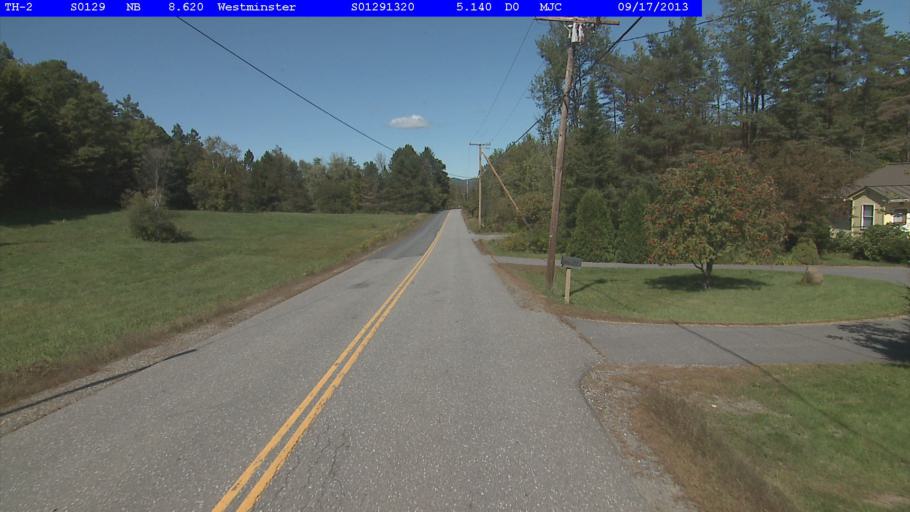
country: US
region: Vermont
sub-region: Windham County
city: Bellows Falls
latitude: 43.0890
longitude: -72.5354
